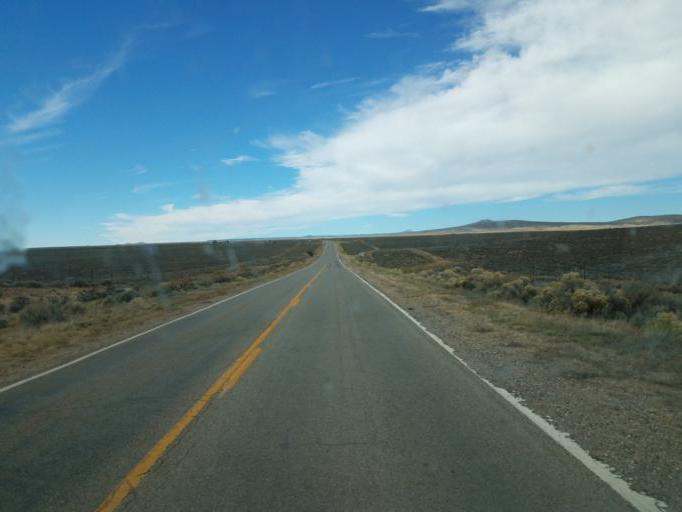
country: US
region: New Mexico
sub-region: Taos County
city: Arroyo Seco
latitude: 36.4742
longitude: -105.7169
